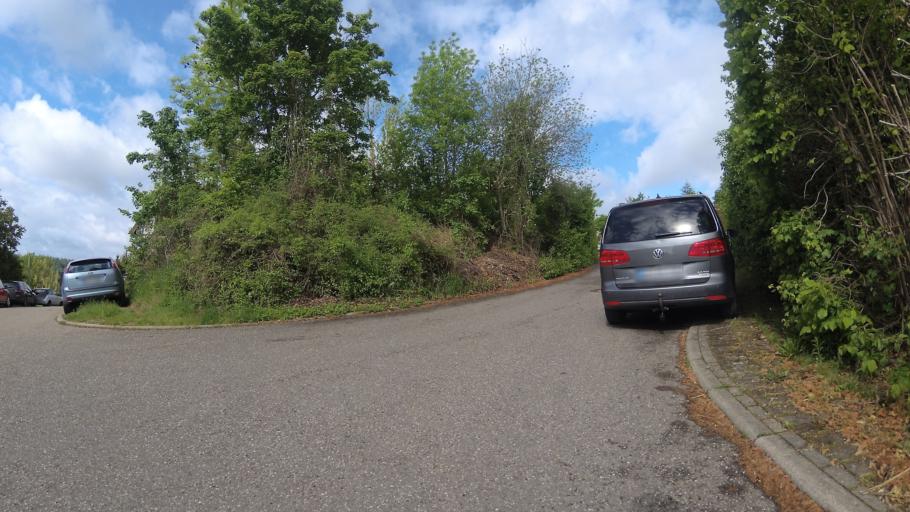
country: DE
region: Baden-Wuerttemberg
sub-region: Regierungsbezirk Stuttgart
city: Erlenbach
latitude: 49.1749
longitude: 9.2651
